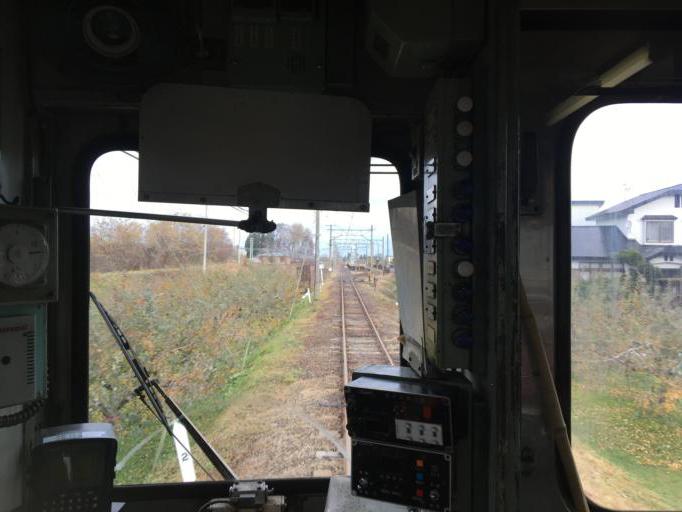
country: JP
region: Aomori
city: Hirosaki
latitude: 40.5341
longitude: 140.5532
